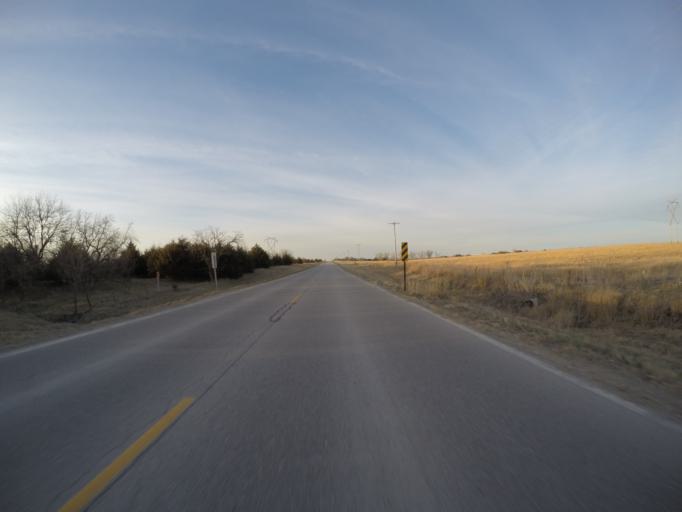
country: US
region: Kansas
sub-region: Riley County
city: Fort Riley North
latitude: 39.3228
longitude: -96.8307
